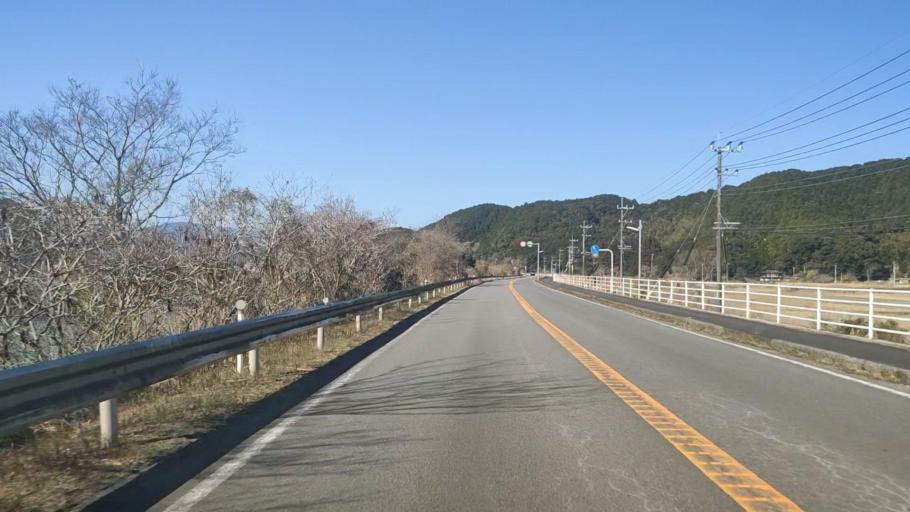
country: JP
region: Oita
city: Saiki
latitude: 32.9372
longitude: 131.9168
